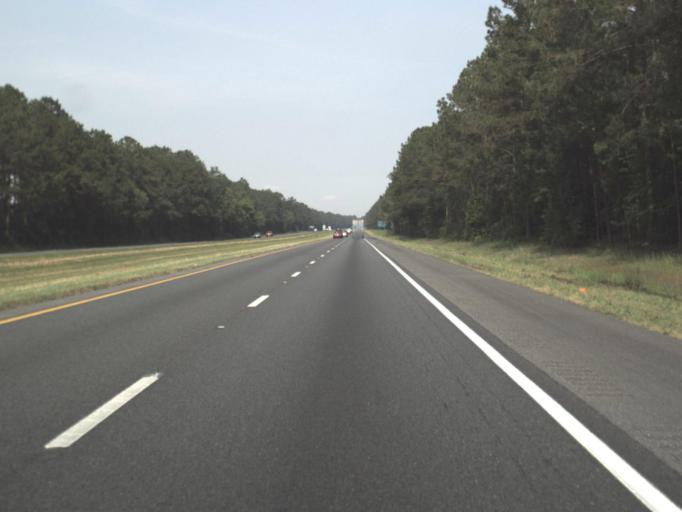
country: US
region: Florida
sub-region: Baker County
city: Macclenny
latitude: 30.2570
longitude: -82.1878
